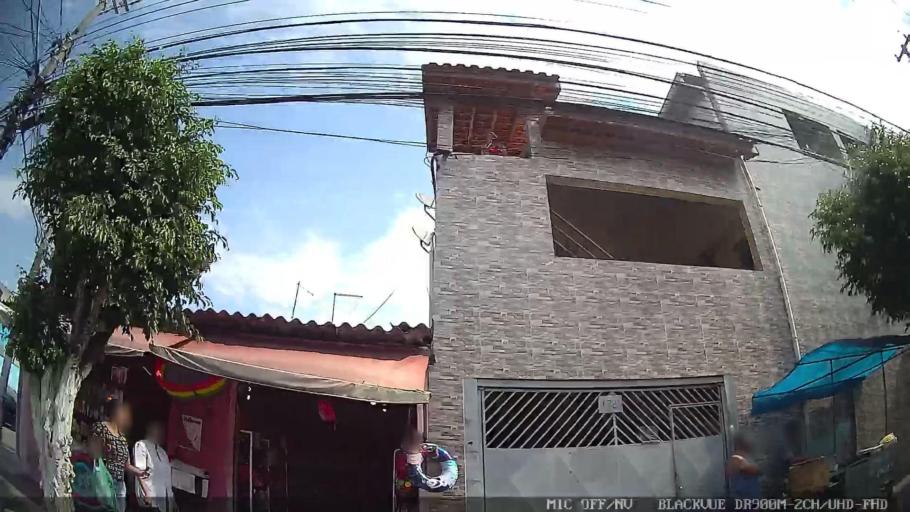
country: BR
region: Sao Paulo
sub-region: Itaquaquecetuba
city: Itaquaquecetuba
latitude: -23.4840
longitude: -46.4173
